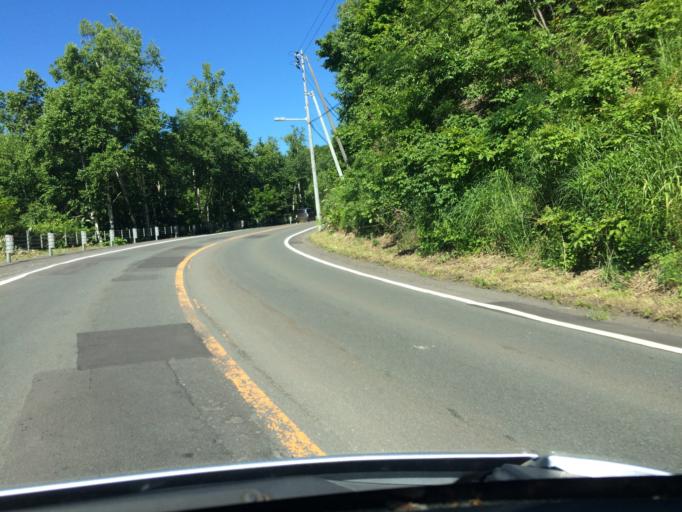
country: JP
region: Hokkaido
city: Sapporo
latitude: 43.0202
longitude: 141.2971
